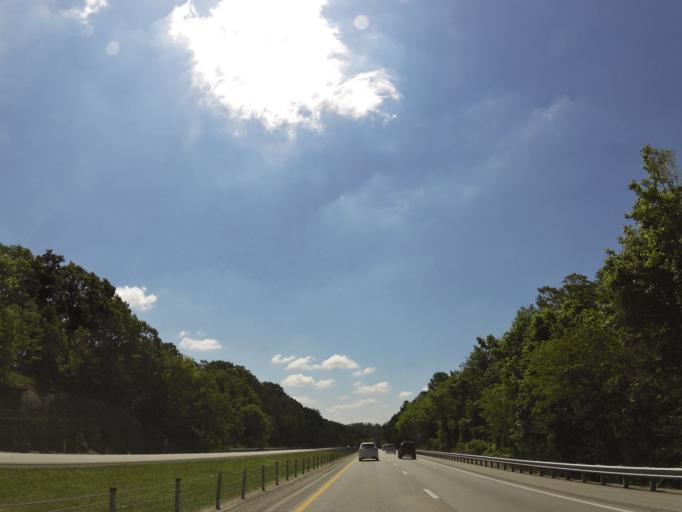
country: US
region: Kentucky
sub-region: Rockcastle County
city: Mount Vernon
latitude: 37.3046
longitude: -84.2850
